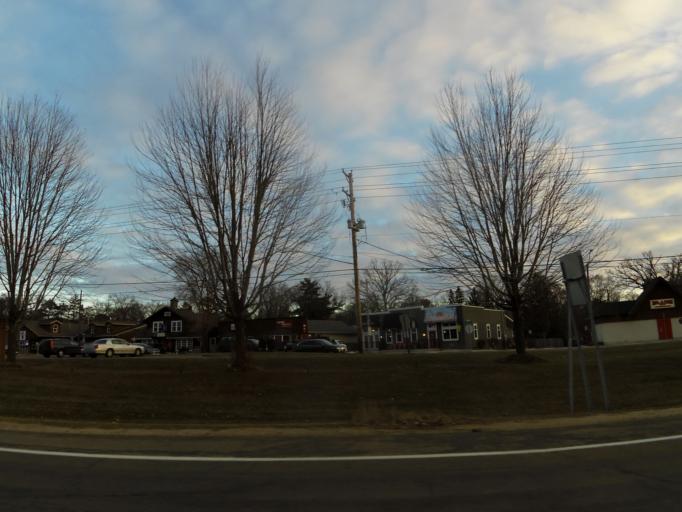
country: US
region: Minnesota
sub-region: Washington County
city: Mahtomedi
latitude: 45.0570
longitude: -92.9598
